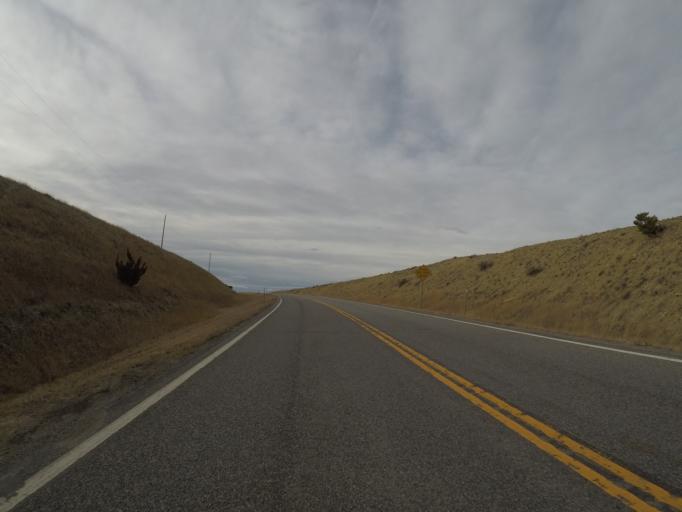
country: US
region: Montana
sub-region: Yellowstone County
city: Laurel
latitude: 45.8563
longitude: -108.7635
